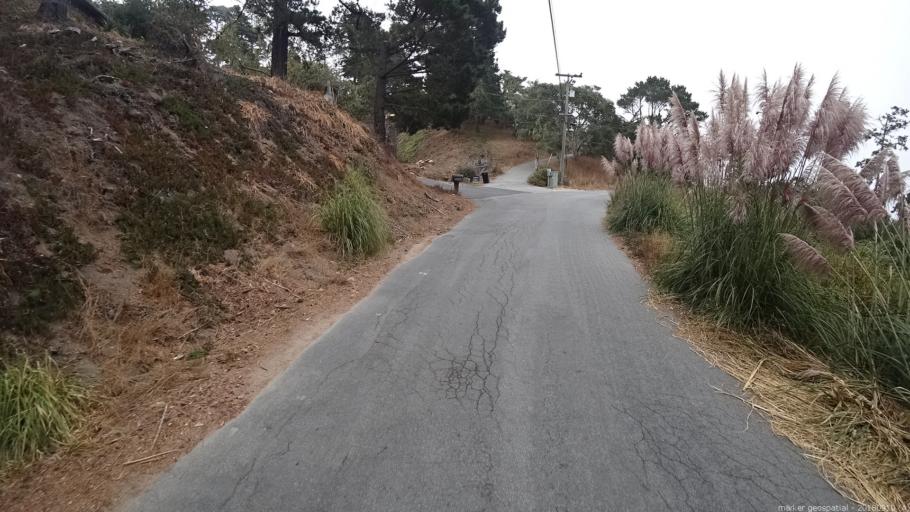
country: US
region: California
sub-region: Monterey County
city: Carmel-by-the-Sea
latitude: 36.4893
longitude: -121.9363
